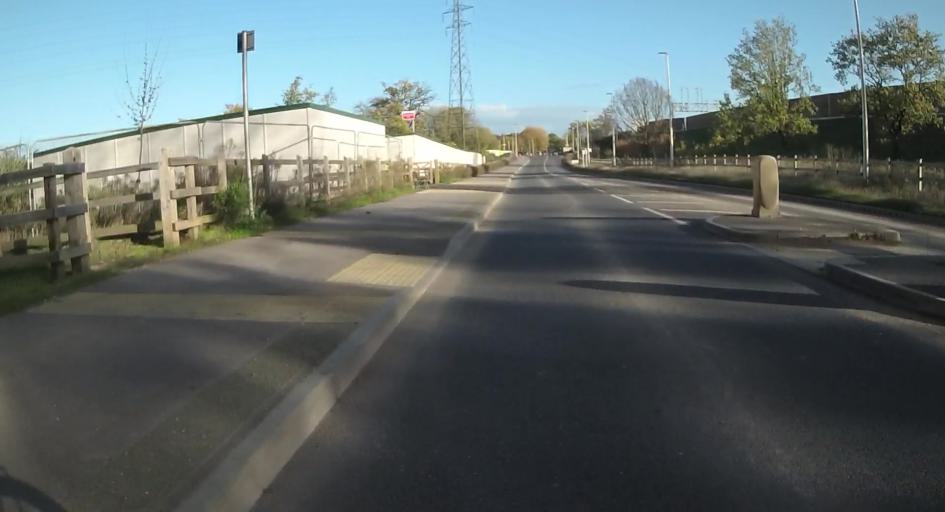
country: GB
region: England
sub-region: Wokingham
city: Winnersh
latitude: 51.4254
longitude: -0.8853
